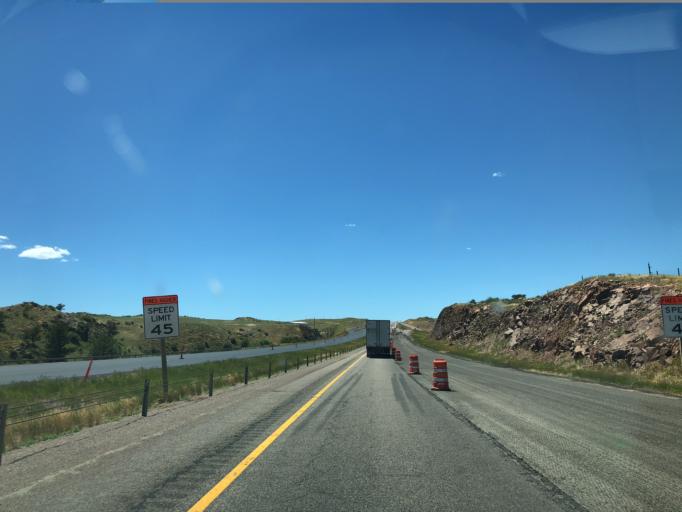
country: US
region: Wyoming
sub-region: Laramie County
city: Cheyenne
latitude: 41.0981
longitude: -105.1642
